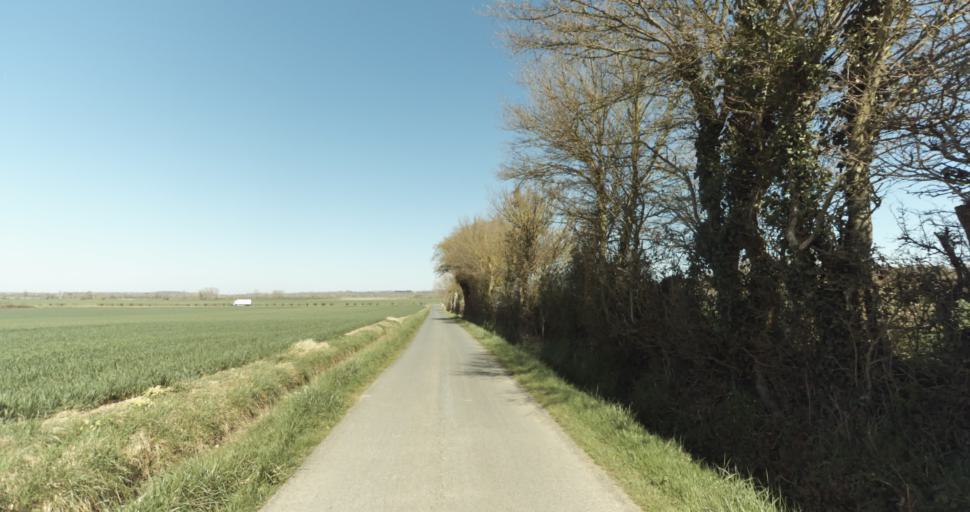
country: FR
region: Lower Normandy
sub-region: Departement du Calvados
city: Saint-Pierre-sur-Dives
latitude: 49.0154
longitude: 0.0296
